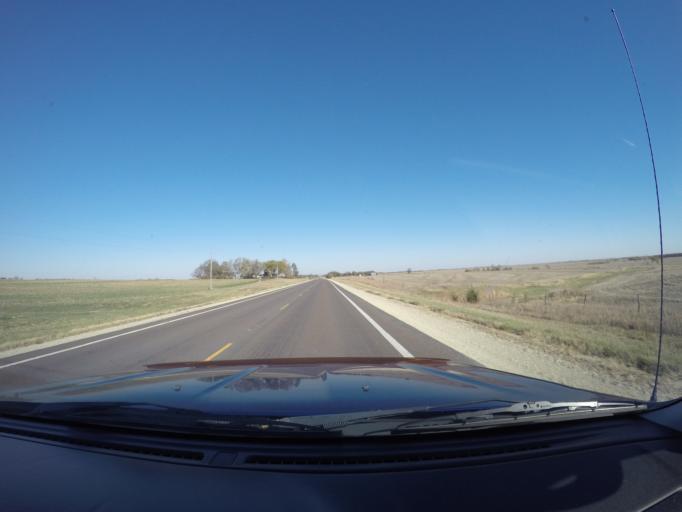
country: US
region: Kansas
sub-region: Marshall County
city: Blue Rapids
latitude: 39.6043
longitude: -96.7501
